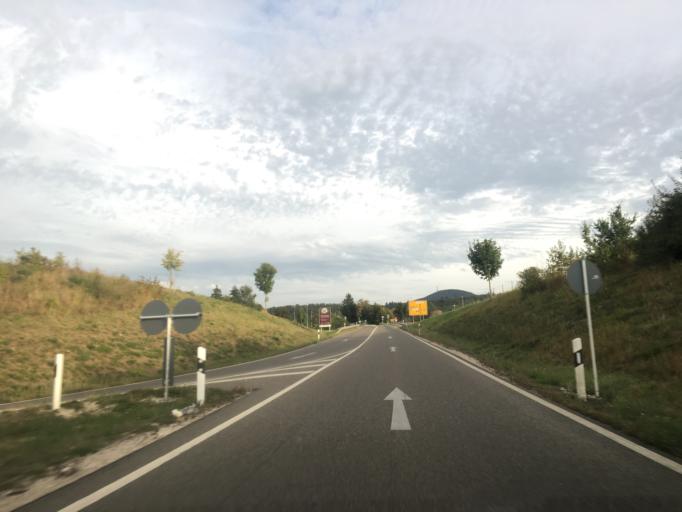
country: DE
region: Baden-Wuerttemberg
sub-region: Tuebingen Region
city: Metzingen
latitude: 48.5289
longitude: 9.2716
